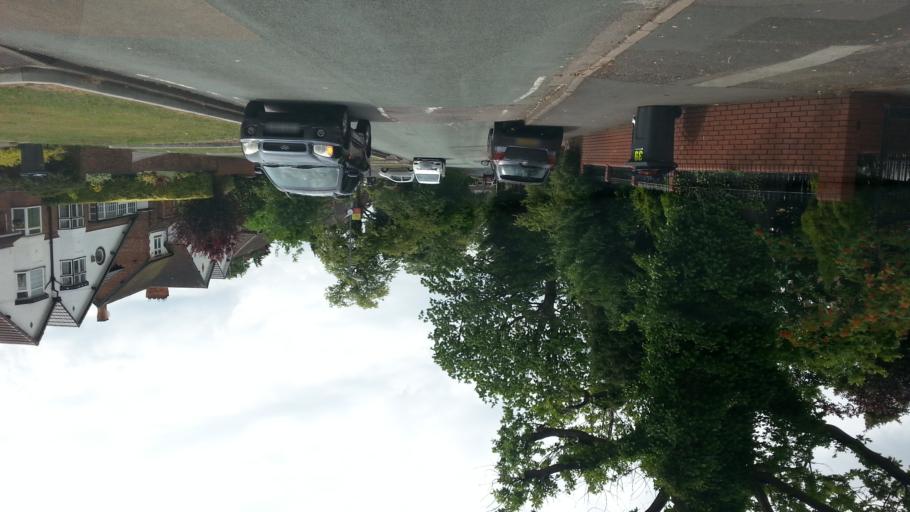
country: GB
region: England
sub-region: City and Borough of Birmingham
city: Acocks Green
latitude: 52.4730
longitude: -1.8066
